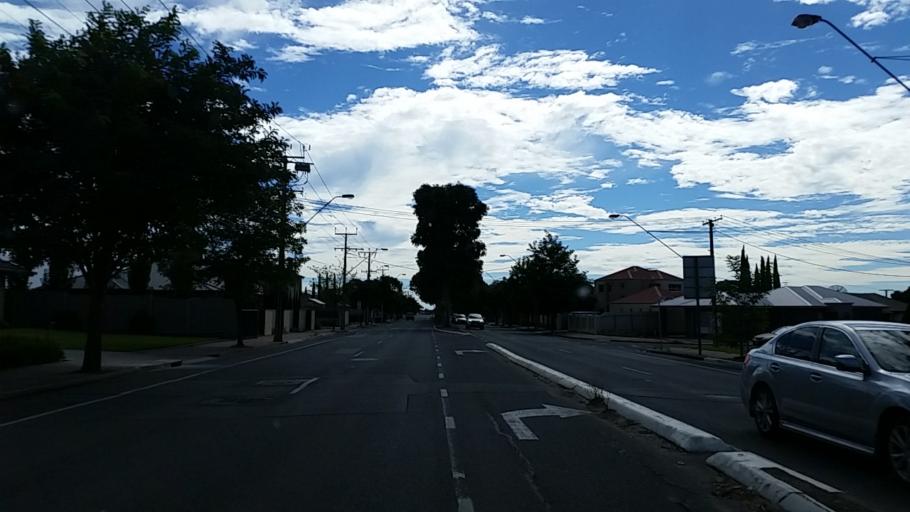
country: AU
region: South Australia
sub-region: Campbelltown
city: Paradise
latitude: -34.8765
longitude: 138.6697
